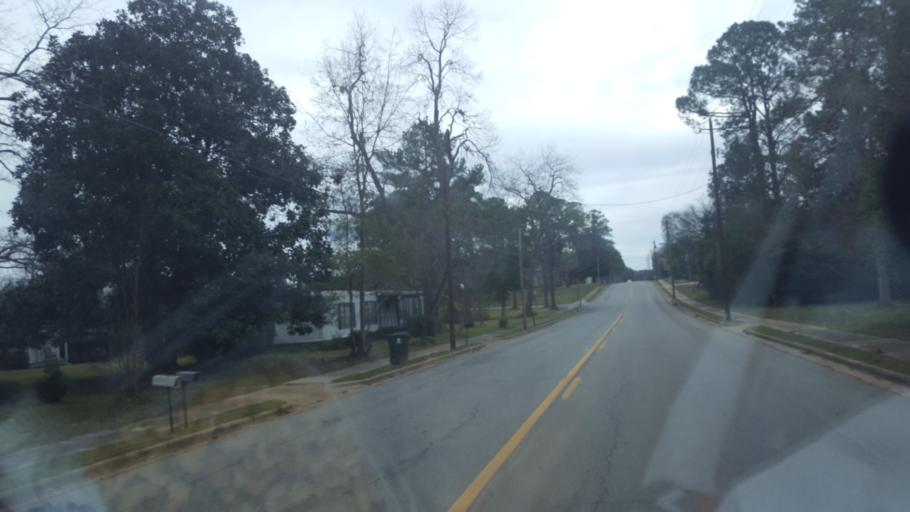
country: US
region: Georgia
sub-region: Wilcox County
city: Rochelle
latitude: 31.8074
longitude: -83.4859
